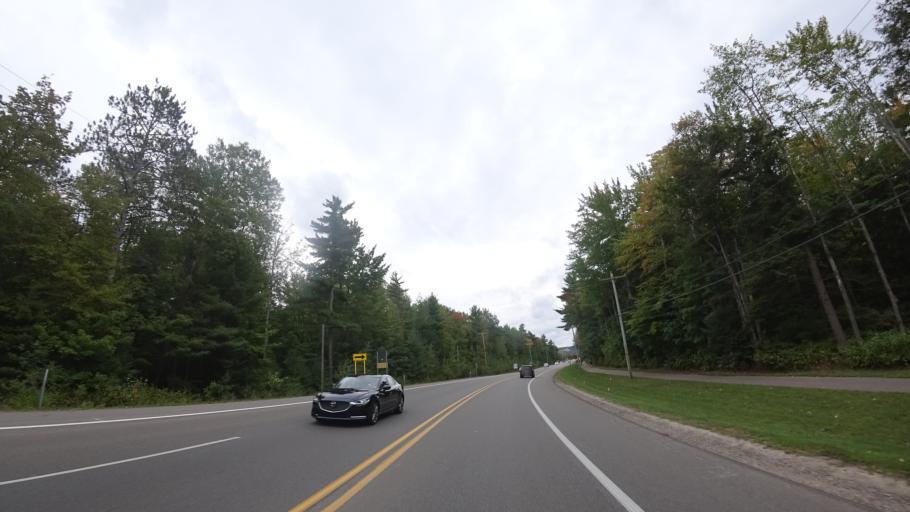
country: US
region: Michigan
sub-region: Emmet County
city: Petoskey
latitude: 45.4102
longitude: -84.9024
